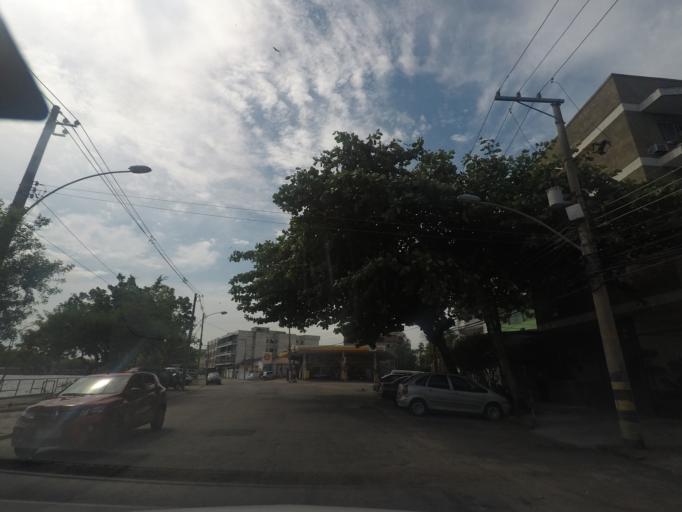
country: BR
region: Rio de Janeiro
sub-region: Rio De Janeiro
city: Rio de Janeiro
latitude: -22.8243
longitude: -43.1735
